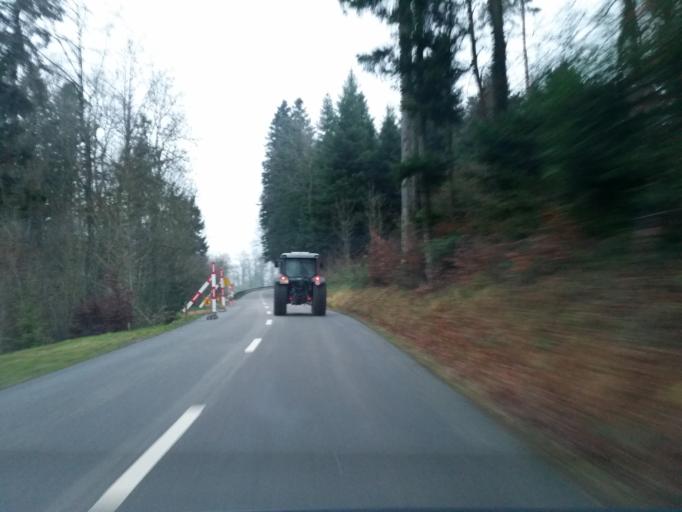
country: CH
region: Thurgau
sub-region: Weinfelden District
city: Sulgen
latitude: 47.5280
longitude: 9.2107
